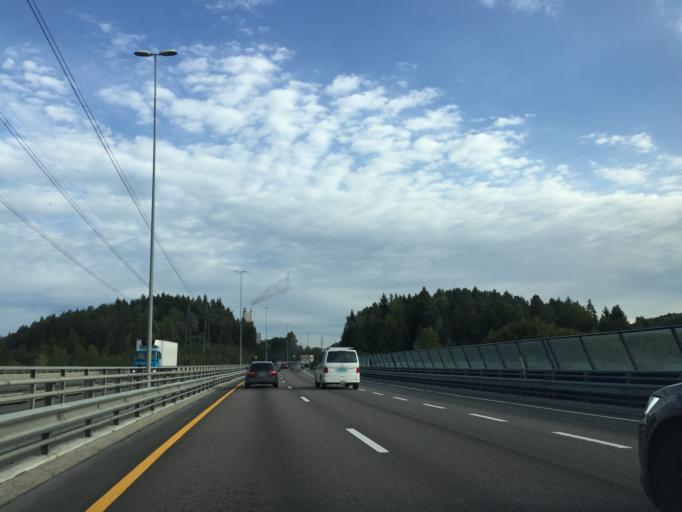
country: NO
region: Akershus
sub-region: Oppegard
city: Kolbotn
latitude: 59.8338
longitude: 10.8402
